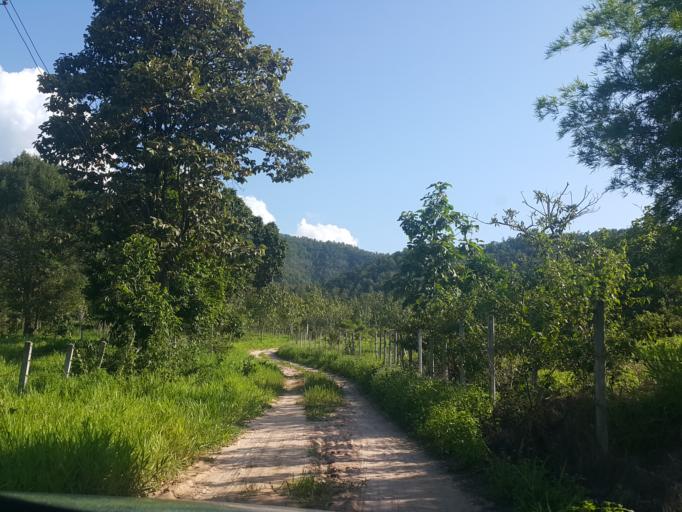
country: TH
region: Chiang Mai
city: Mae On
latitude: 18.7119
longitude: 99.2126
